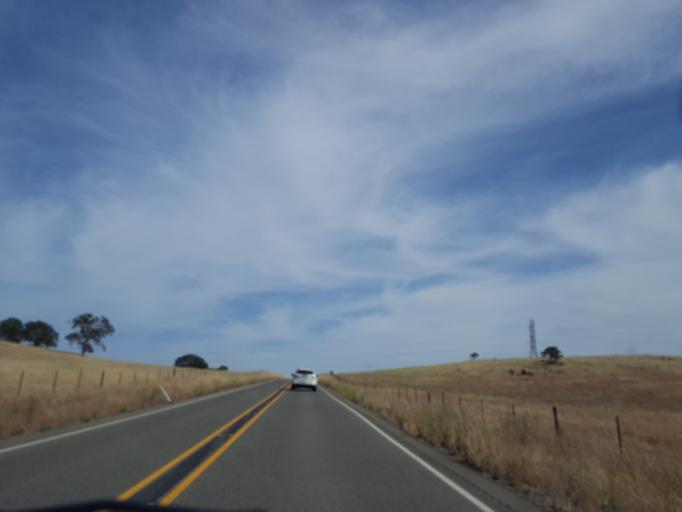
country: US
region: California
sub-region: Tuolumne County
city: Jamestown
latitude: 37.7906
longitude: -120.4657
